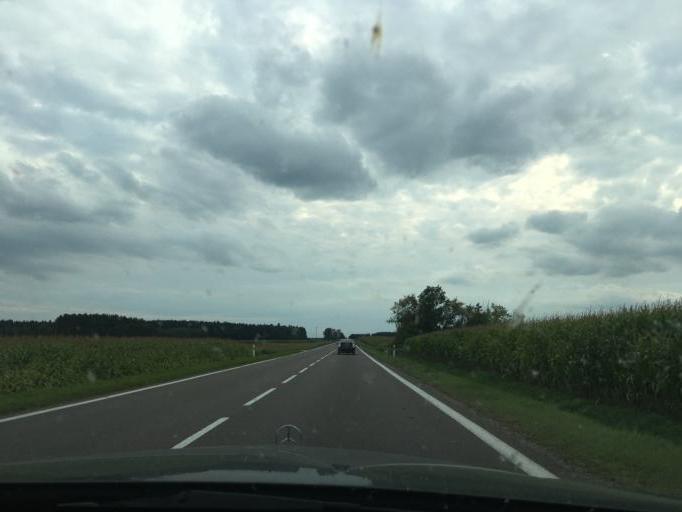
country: PL
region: Podlasie
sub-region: Powiat grajewski
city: Szczuczyn
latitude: 53.4831
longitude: 22.2165
